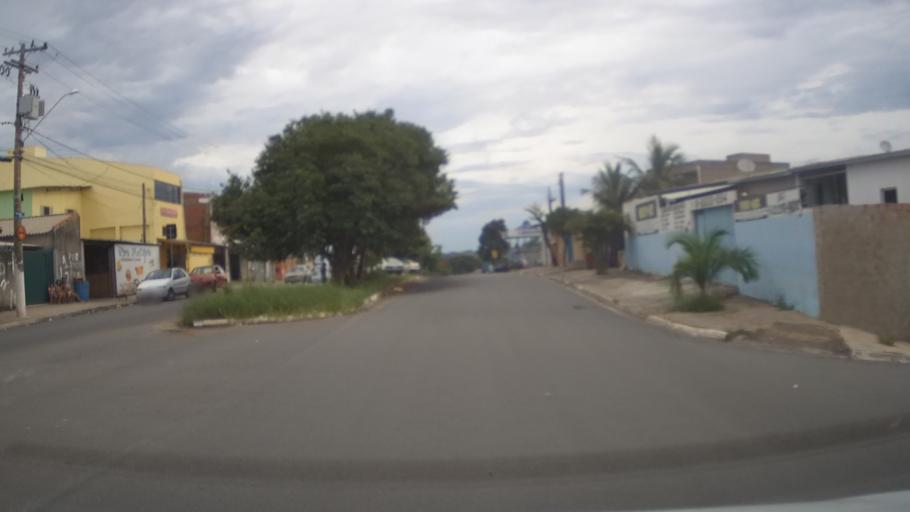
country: BR
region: Sao Paulo
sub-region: Hortolandia
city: Hortolandia
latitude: -22.9592
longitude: -47.1835
